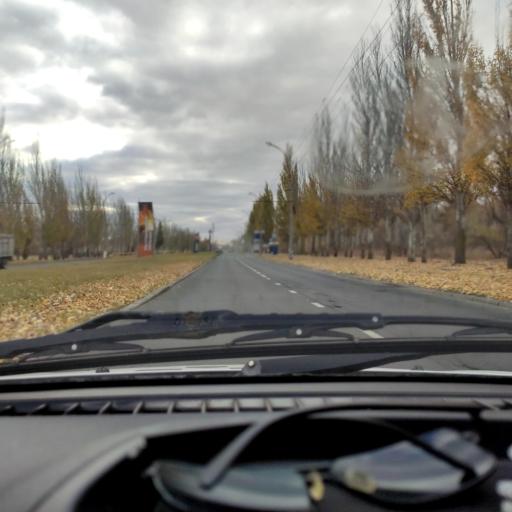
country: RU
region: Samara
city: Tol'yatti
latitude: 53.5484
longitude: 49.2727
